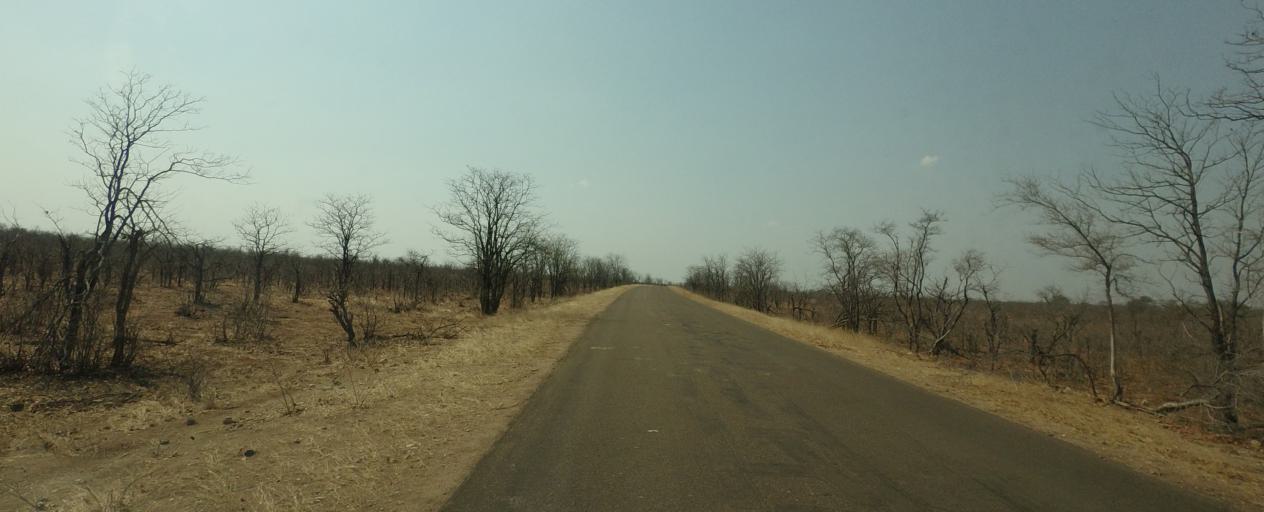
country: ZA
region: Limpopo
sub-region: Mopani District Municipality
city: Giyani
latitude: -23.2364
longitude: 31.3137
